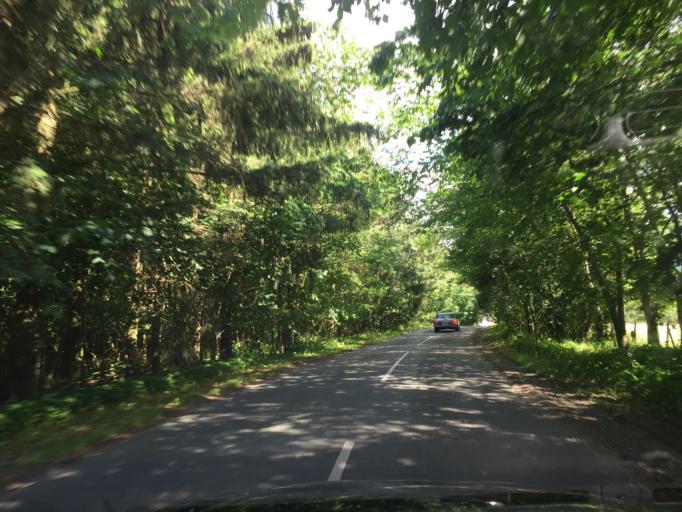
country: DK
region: Capital Region
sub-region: Egedal Kommune
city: Vekso
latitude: 55.7144
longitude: 12.2528
